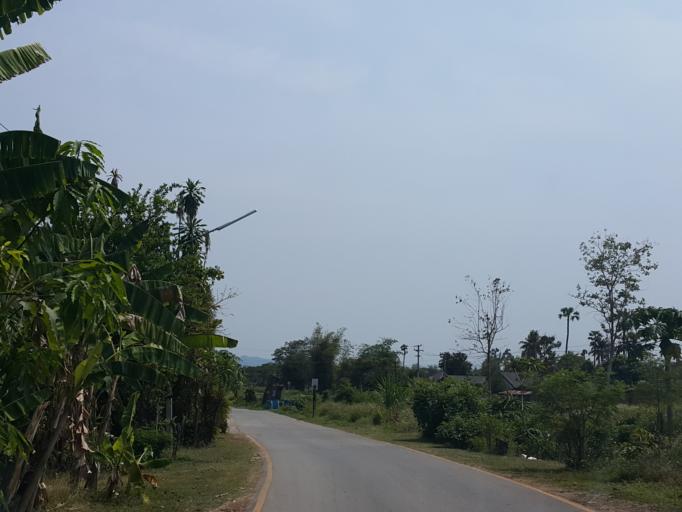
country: TH
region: Lampang
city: Lampang
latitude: 18.3044
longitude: 99.4280
